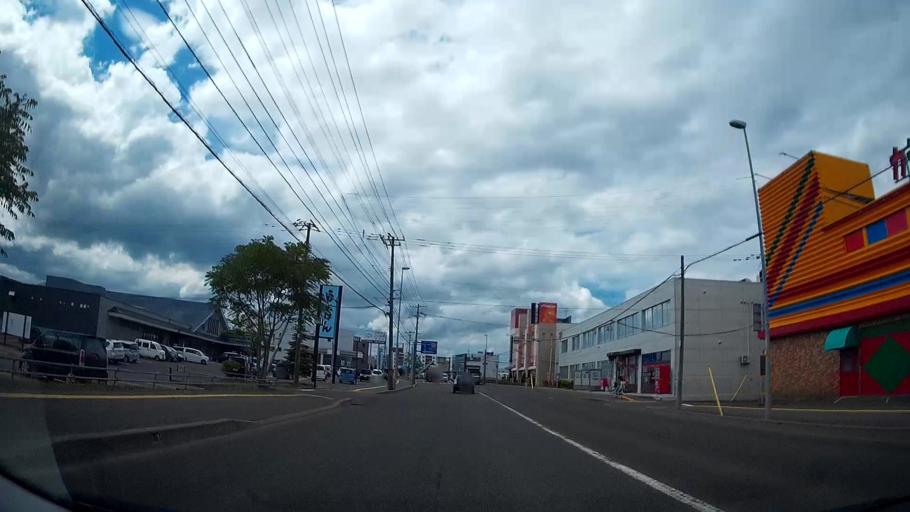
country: JP
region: Hokkaido
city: Chitose
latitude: 42.8758
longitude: 141.5831
